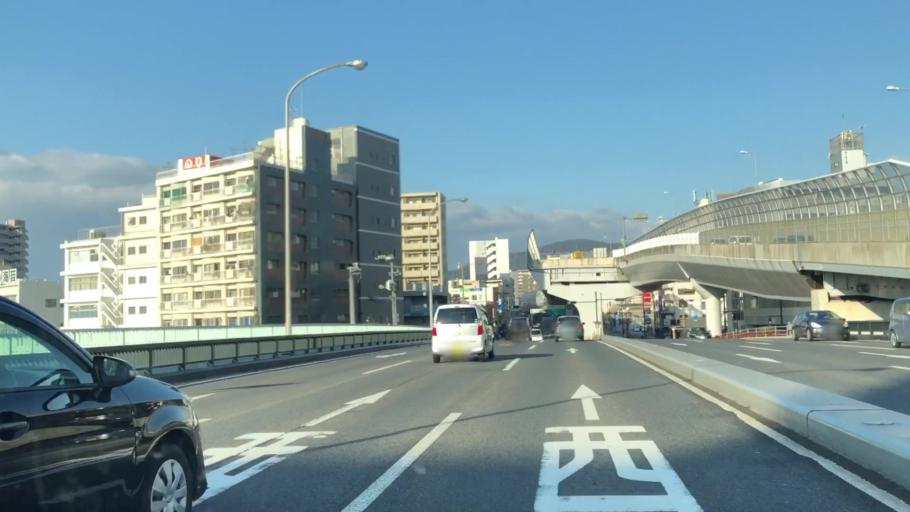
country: JP
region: Hiroshima
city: Hiroshima-shi
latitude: 34.3872
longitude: 132.4402
